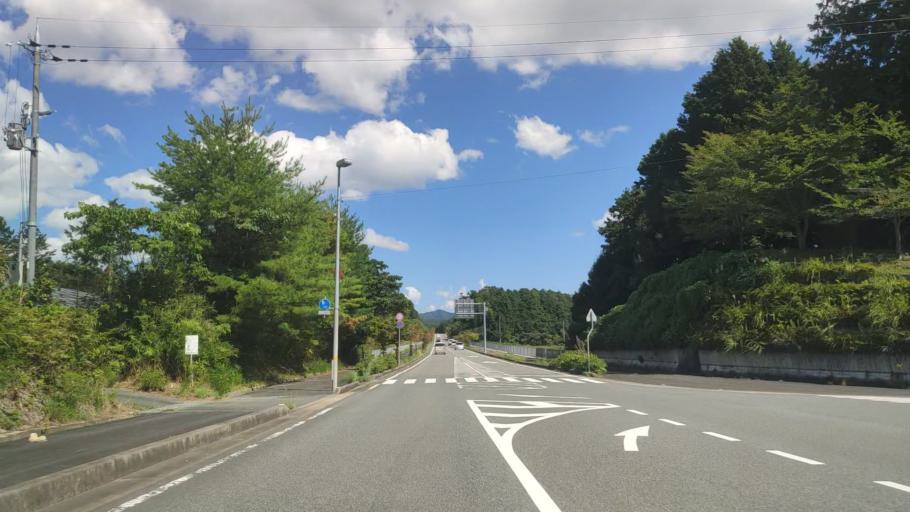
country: JP
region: Kyoto
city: Fukuchiyama
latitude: 35.2478
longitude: 135.1321
